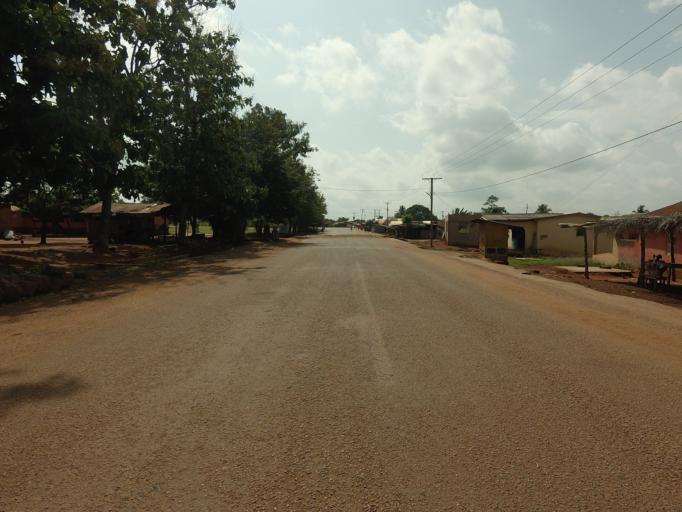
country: TG
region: Maritime
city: Tsevie
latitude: 6.3595
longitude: 0.8661
